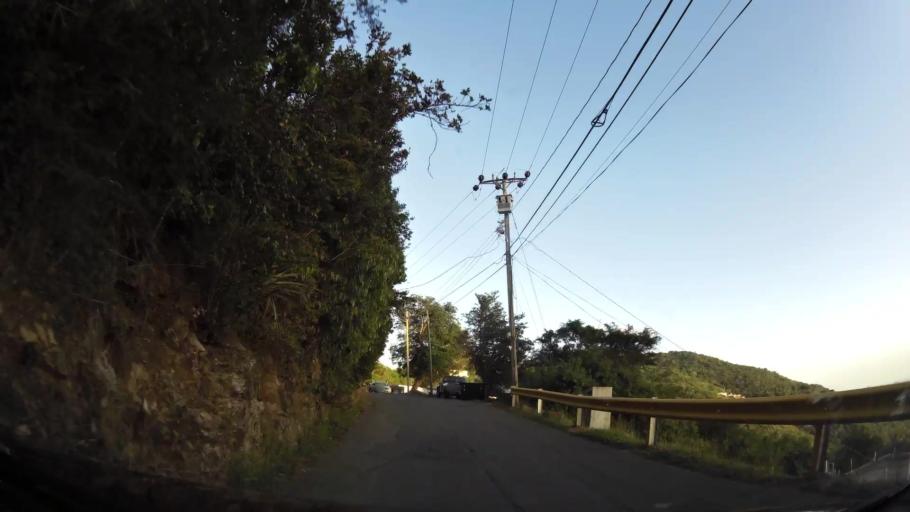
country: VG
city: Tortola
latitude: 18.4425
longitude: -64.6087
